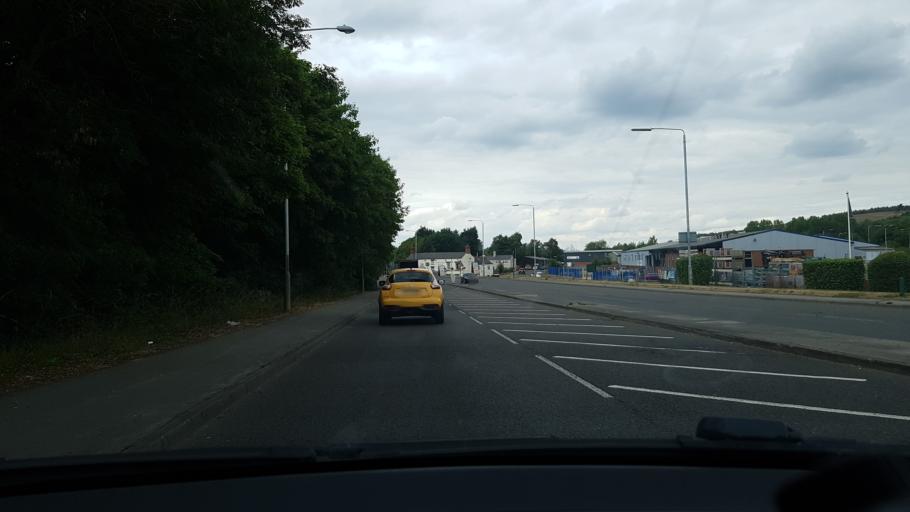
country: GB
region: England
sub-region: Nottinghamshire
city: Eastwood
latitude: 53.0180
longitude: -1.3222
